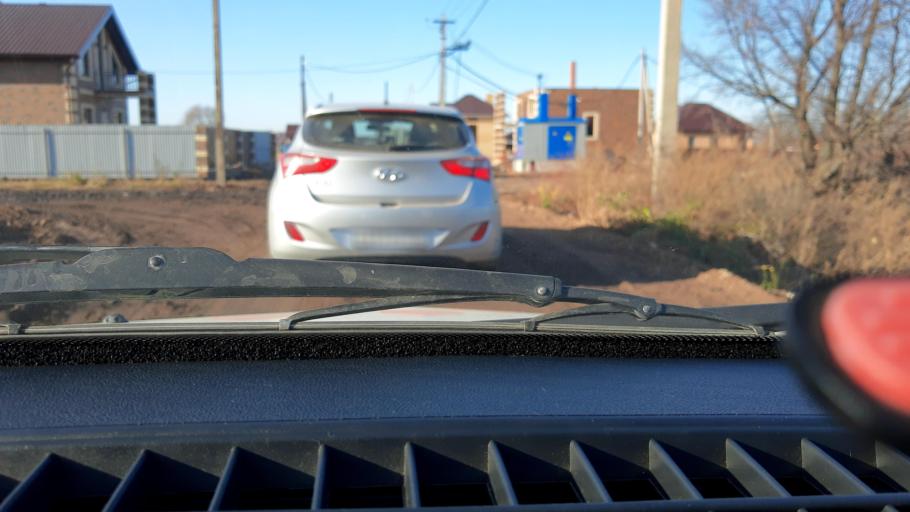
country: RU
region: Bashkortostan
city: Kabakovo
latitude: 54.6272
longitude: 56.1298
